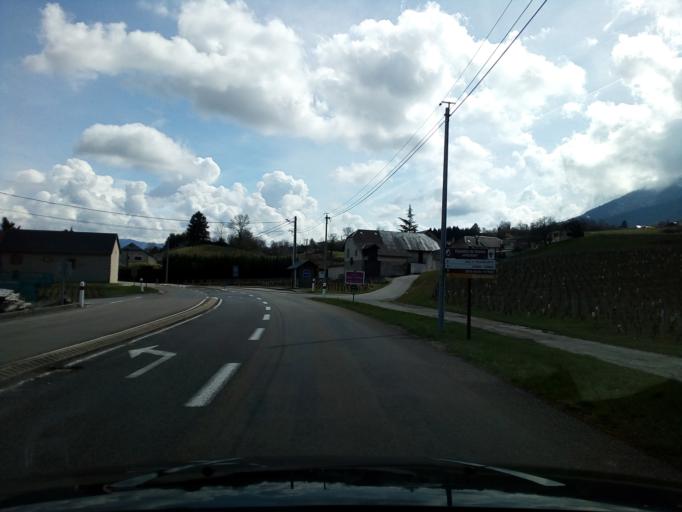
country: FR
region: Rhone-Alpes
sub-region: Departement de la Savoie
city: Saint-Baldoph
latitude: 45.5064
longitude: 5.9603
